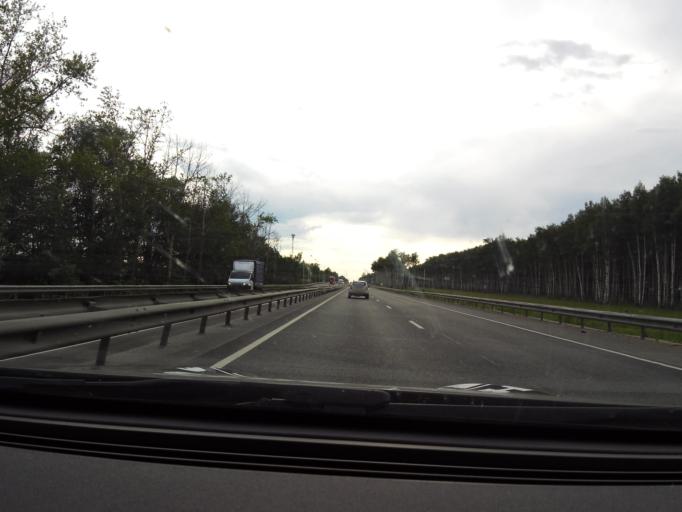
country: RU
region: Vladimir
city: Luknovo
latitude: 56.2388
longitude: 42.0511
